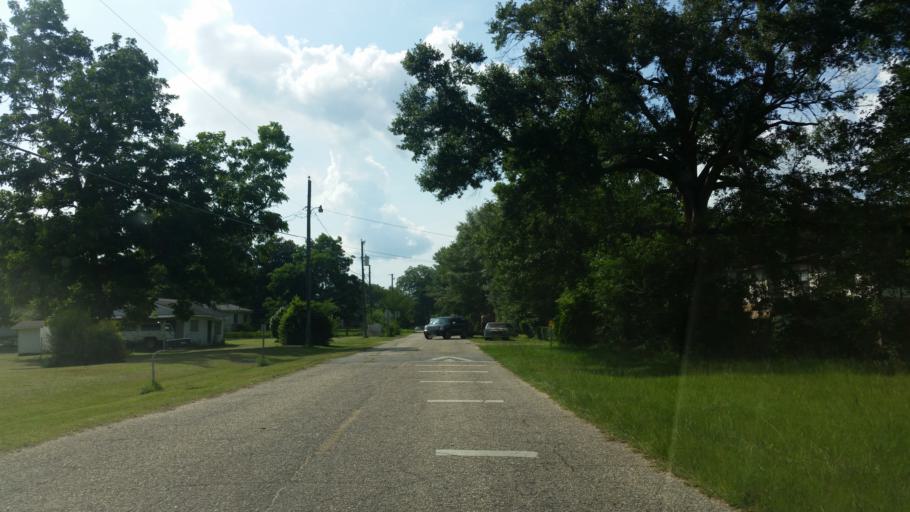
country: US
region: Florida
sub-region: Escambia County
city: Gonzalez
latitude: 30.5895
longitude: -87.3024
